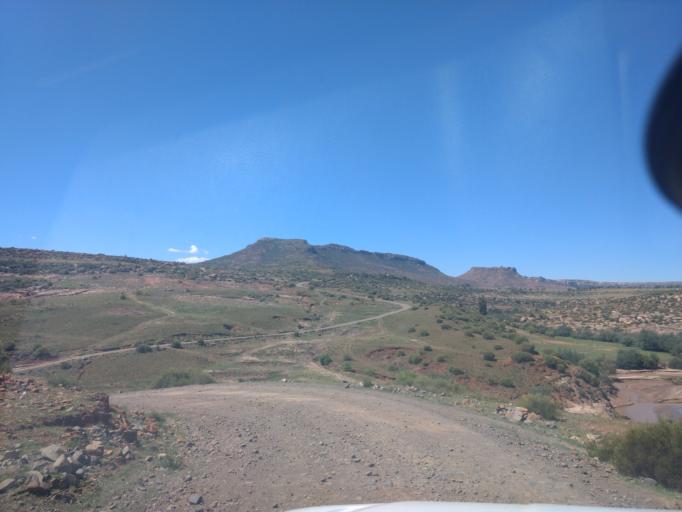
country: LS
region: Maseru
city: Maseru
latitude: -29.4844
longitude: 27.3707
